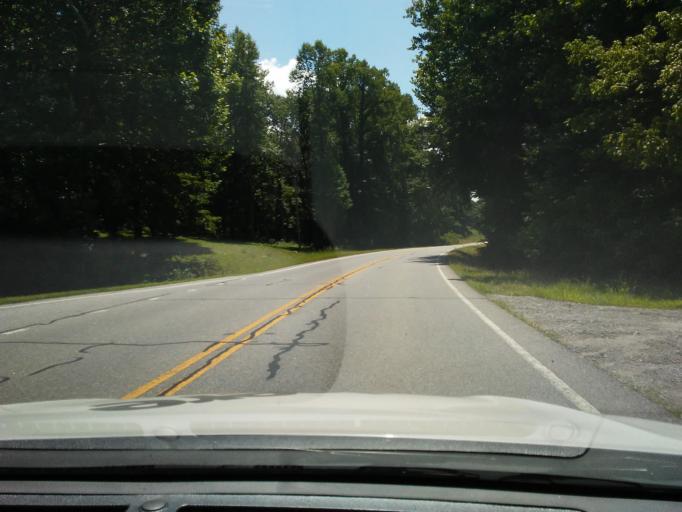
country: US
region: Georgia
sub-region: Towns County
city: Hiawassee
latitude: 34.9672
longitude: -83.7417
